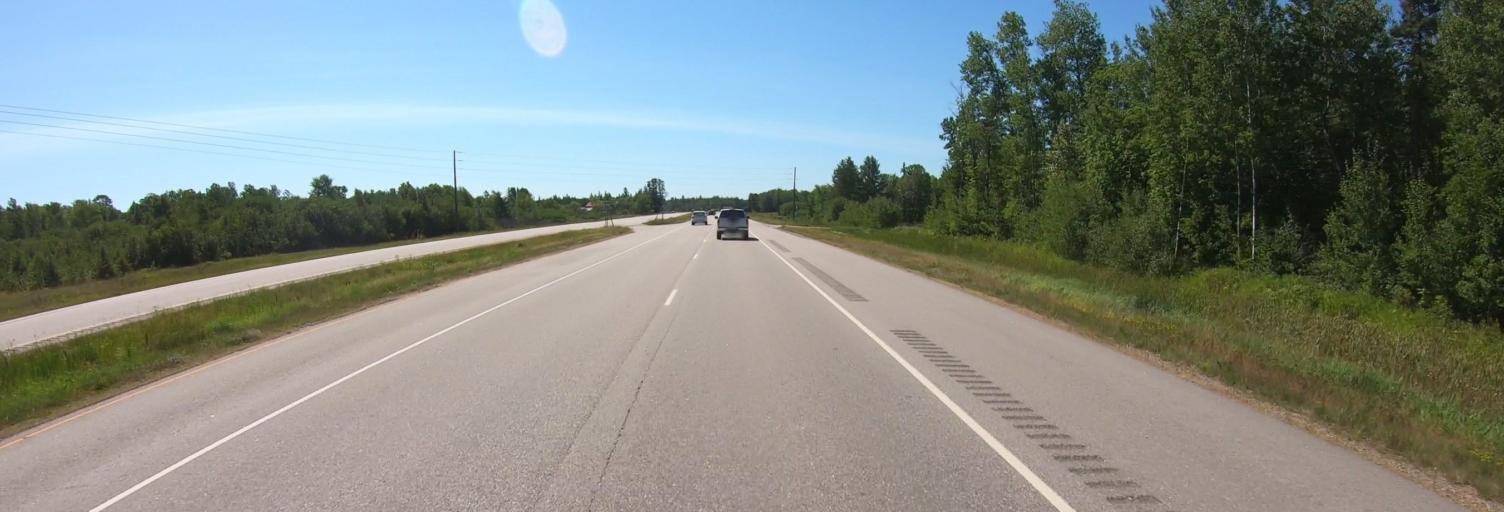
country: US
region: Minnesota
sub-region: Saint Louis County
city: Mountain Iron
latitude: 47.8122
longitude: -92.6746
